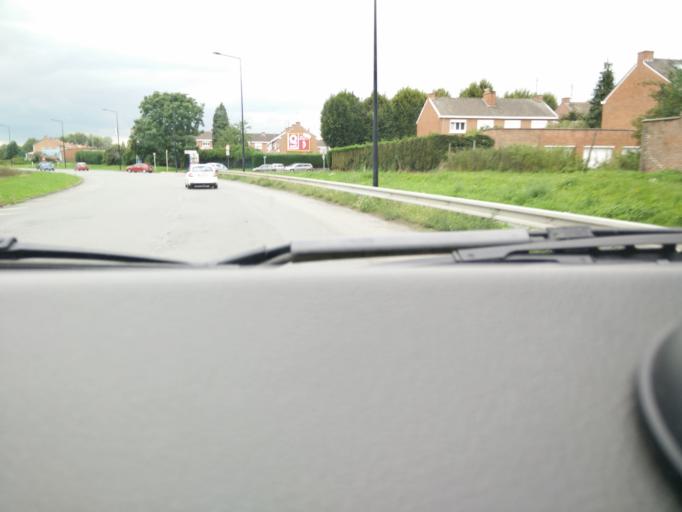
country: FR
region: Nord-Pas-de-Calais
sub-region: Departement du Nord
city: La Sentinelle
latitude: 50.3563
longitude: 3.4943
